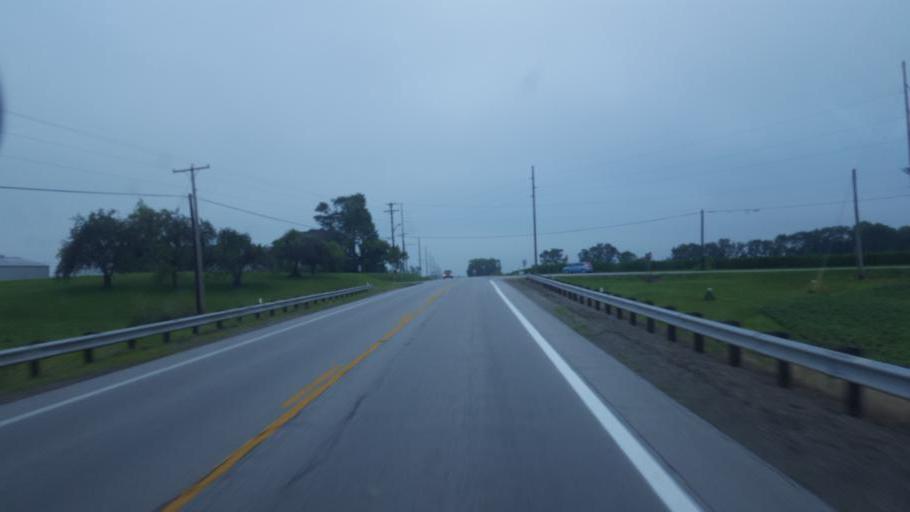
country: US
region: Ohio
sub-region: Fayette County
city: Washington Court House
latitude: 39.5917
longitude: -83.3869
